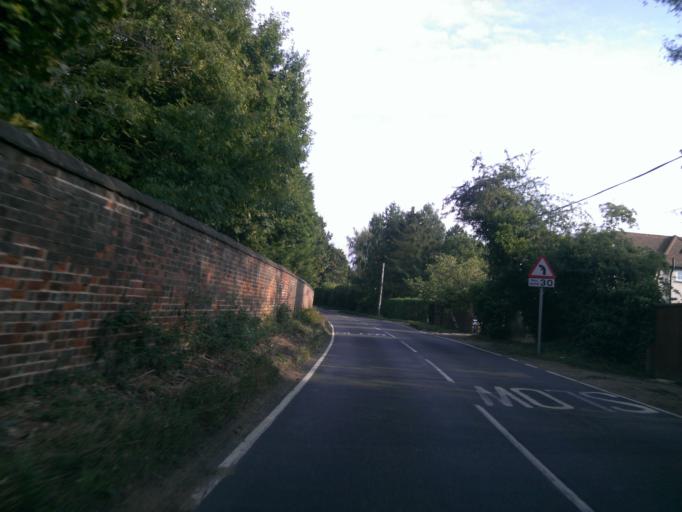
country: GB
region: England
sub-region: Essex
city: Great Totham
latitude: 51.8042
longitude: 0.6829
